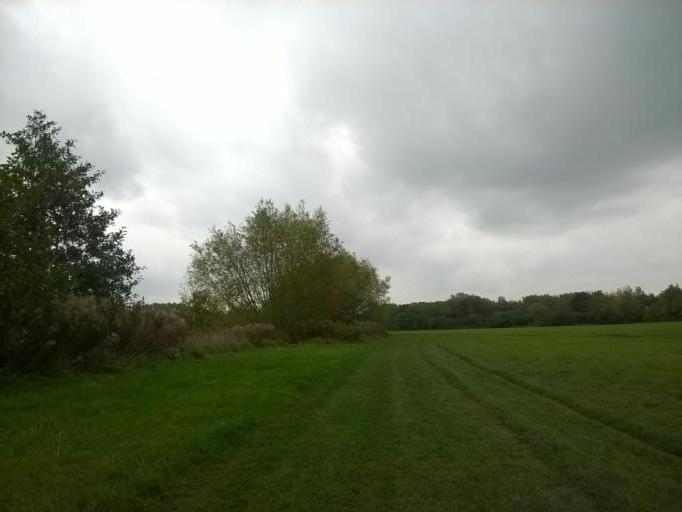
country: GB
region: England
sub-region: Wokingham
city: Sonning
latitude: 51.4647
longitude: -0.9339
